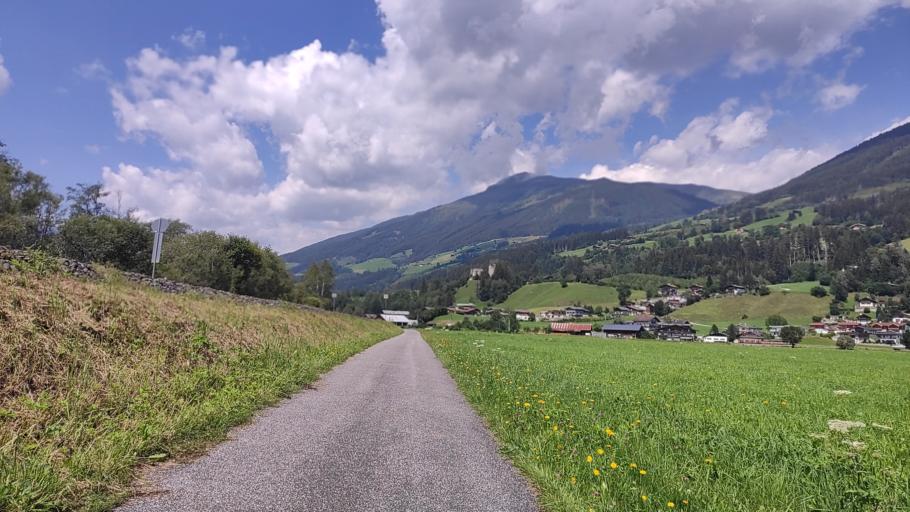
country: AT
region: Salzburg
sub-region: Politischer Bezirk Zell am See
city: Neukirchen am Grossvenediger
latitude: 47.2441
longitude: 12.2547
